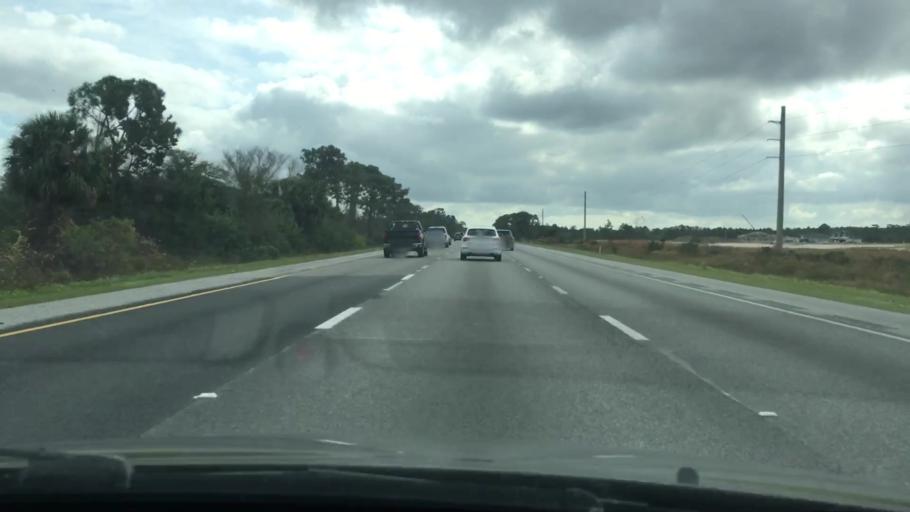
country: US
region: Florida
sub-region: Volusia County
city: Samsula-Spruce Creek
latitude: 29.0807
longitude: -81.0165
